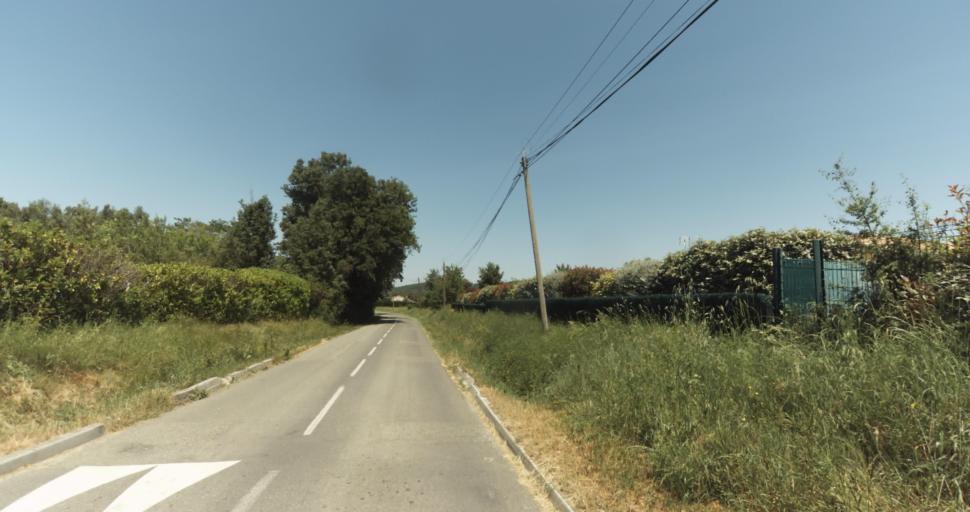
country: FR
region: Midi-Pyrenees
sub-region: Departement de la Haute-Garonne
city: Levignac
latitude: 43.6410
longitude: 1.1734
